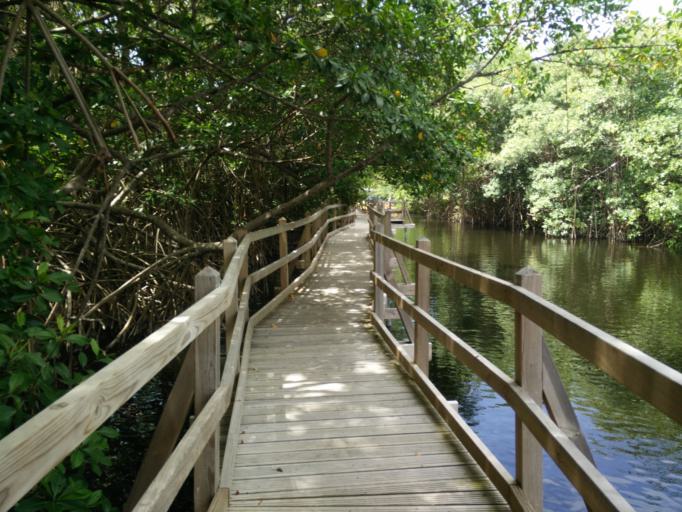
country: GP
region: Guadeloupe
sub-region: Guadeloupe
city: Grand-Bourg
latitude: 15.9873
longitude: -61.3010
